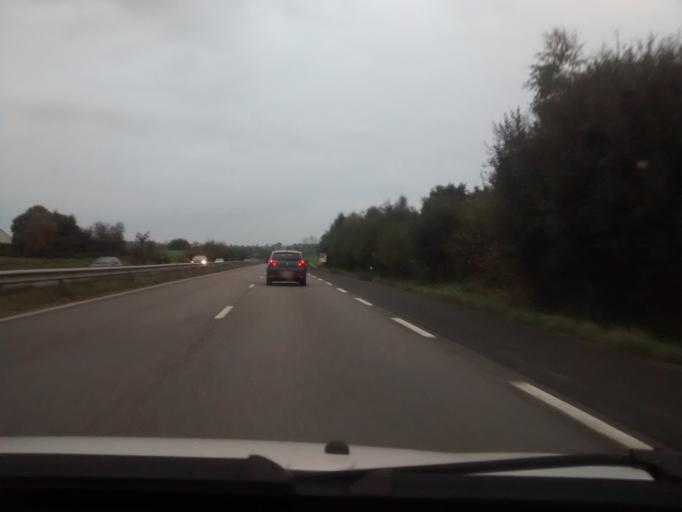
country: FR
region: Brittany
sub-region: Departement d'Ille-et-Vilaine
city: La Meziere
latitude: 48.2403
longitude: -1.7599
